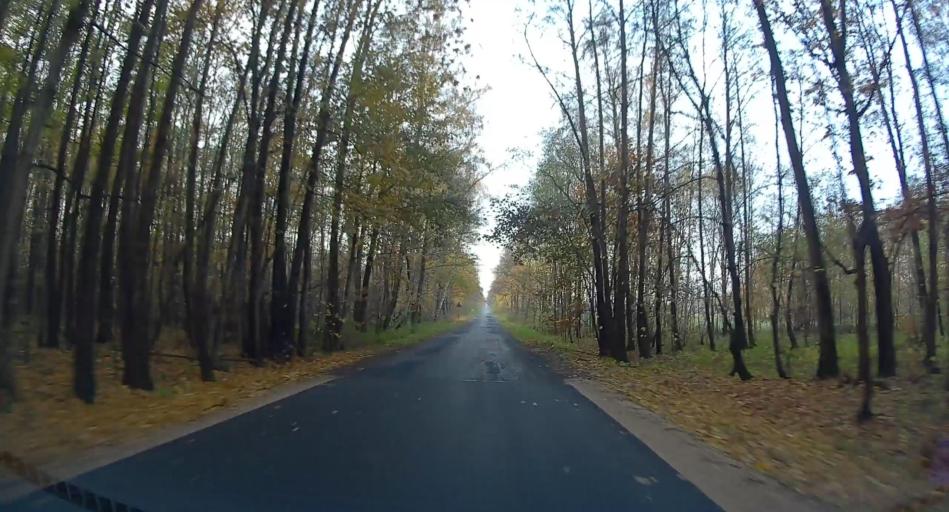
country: PL
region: Masovian Voivodeship
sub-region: Powiat zyrardowski
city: Puszcza Marianska
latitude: 51.9414
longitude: 20.3694
